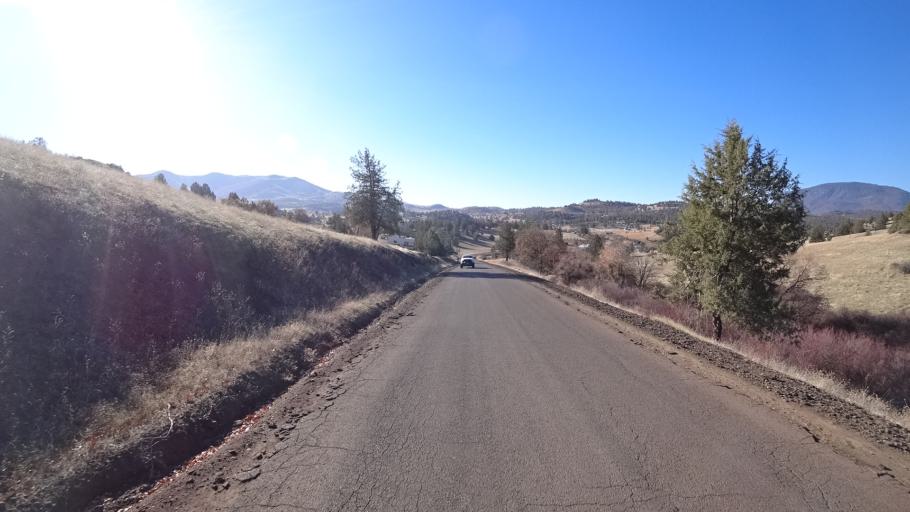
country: US
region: California
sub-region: Siskiyou County
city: Montague
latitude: 41.8975
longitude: -122.4241
